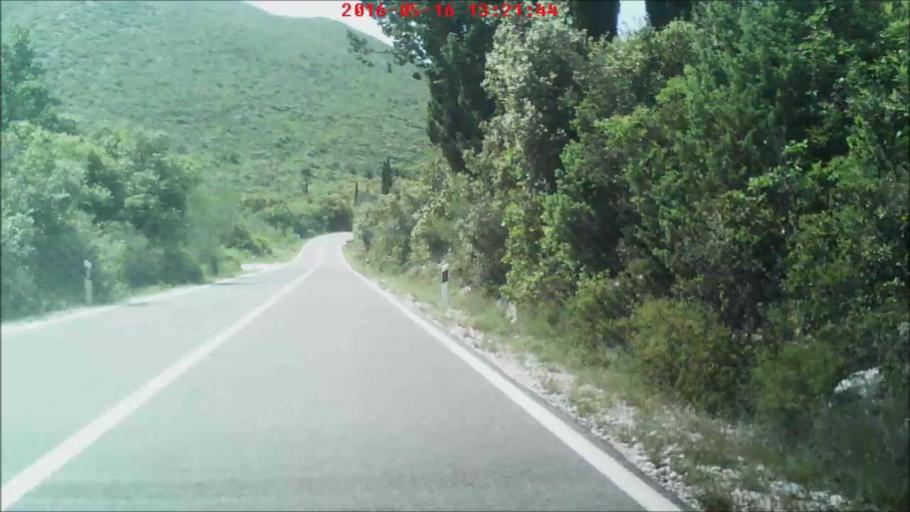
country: HR
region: Dubrovacko-Neretvanska
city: Ston
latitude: 42.8318
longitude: 17.7294
